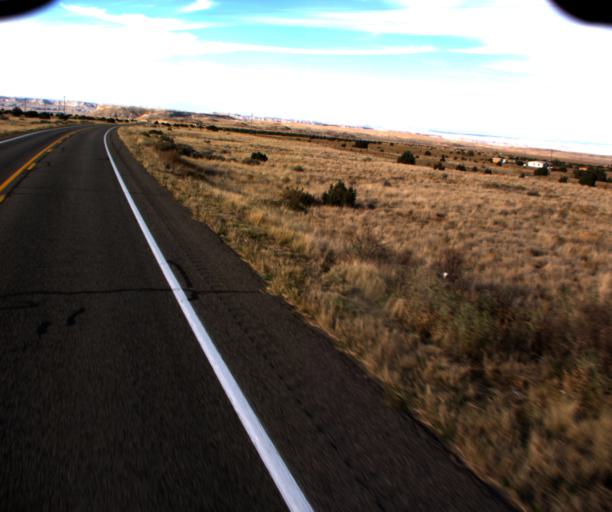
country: US
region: New Mexico
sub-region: San Juan County
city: Shiprock
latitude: 36.8938
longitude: -109.0630
